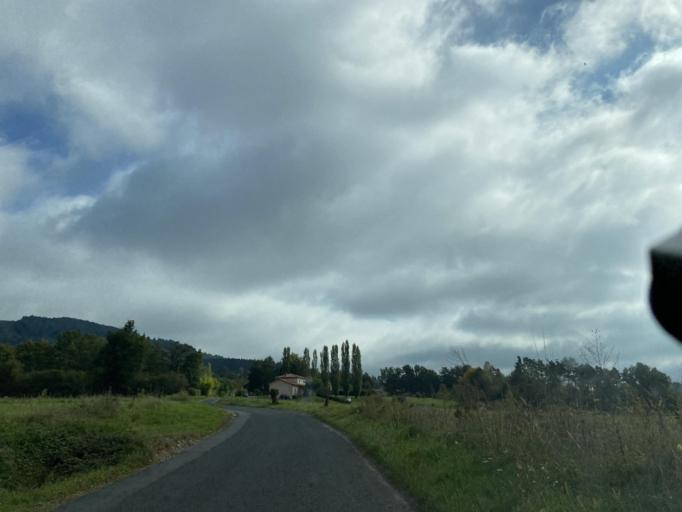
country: FR
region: Auvergne
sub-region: Departement du Puy-de-Dome
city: Escoutoux
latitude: 45.8328
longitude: 3.5412
